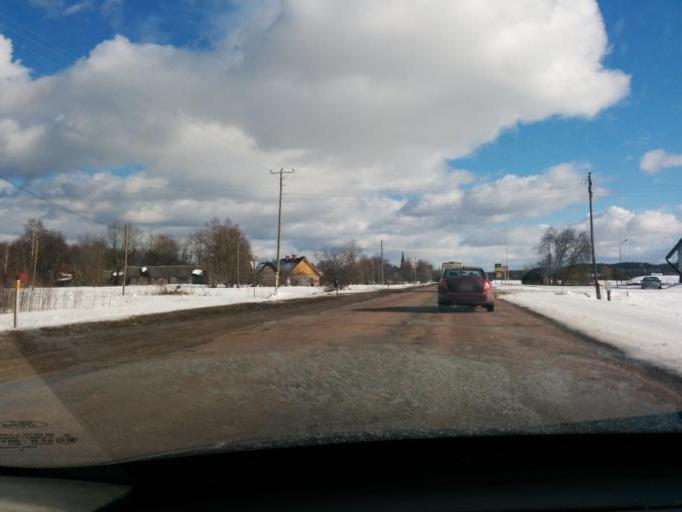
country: LV
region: Cesvaine
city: Cesvaine
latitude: 57.2400
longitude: 26.3901
